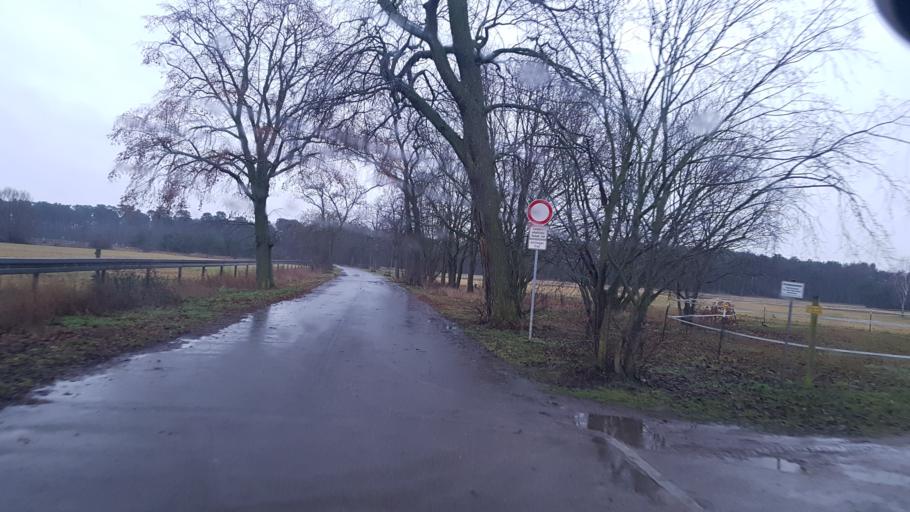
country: DE
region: Brandenburg
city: Ludwigsfelde
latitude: 52.3113
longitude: 13.2046
